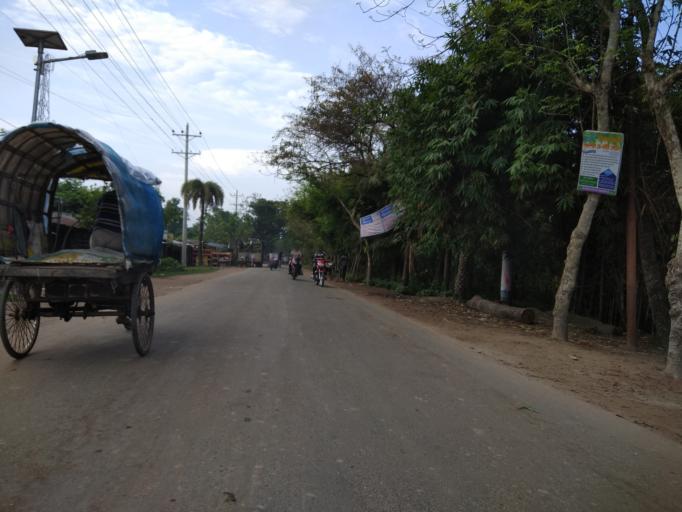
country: IN
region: West Bengal
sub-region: North 24 Parganas
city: Taki
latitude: 22.3418
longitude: 89.1054
